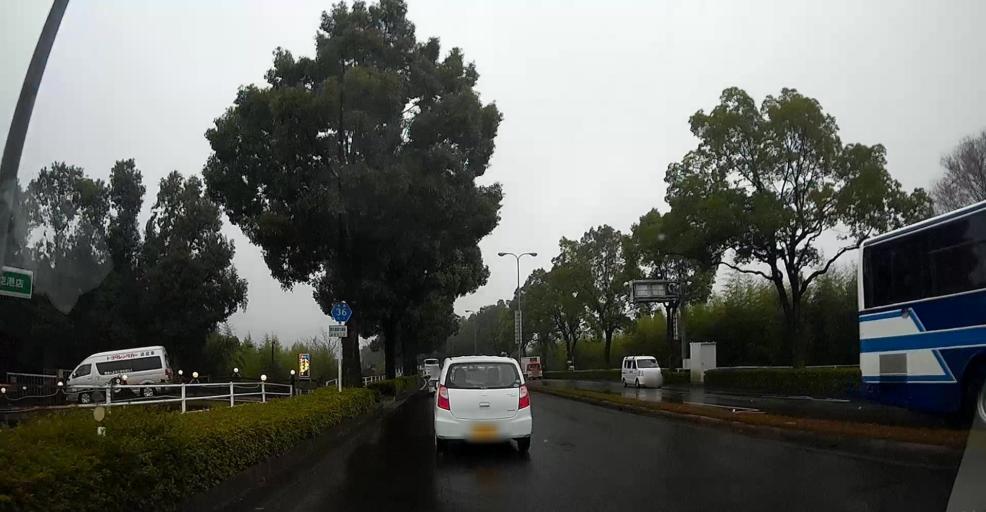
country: JP
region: Kumamoto
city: Ozu
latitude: 32.8320
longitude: 130.8567
